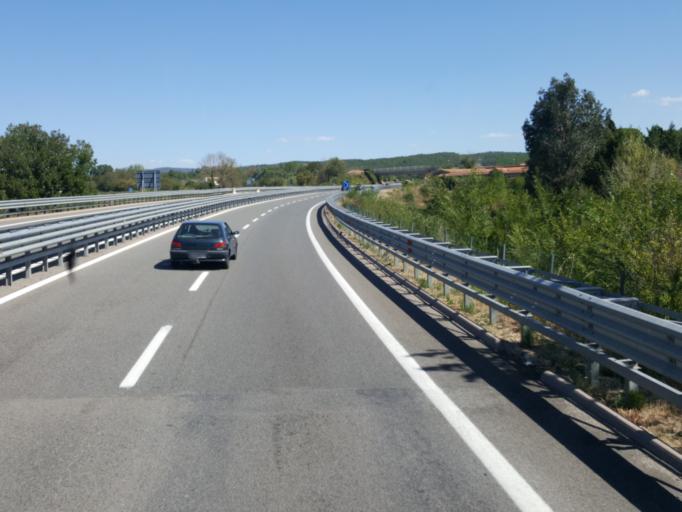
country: IT
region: Tuscany
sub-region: Provincia di Grosseto
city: Campagnatico
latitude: 42.9312
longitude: 11.2661
